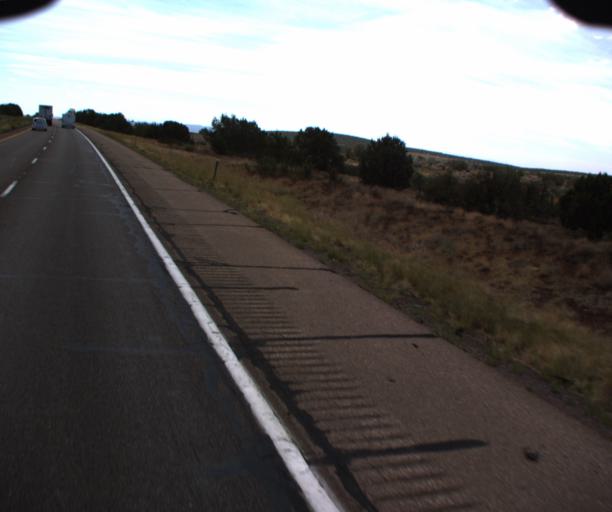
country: US
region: Arizona
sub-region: Yavapai County
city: Paulden
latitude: 35.2637
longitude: -112.7225
